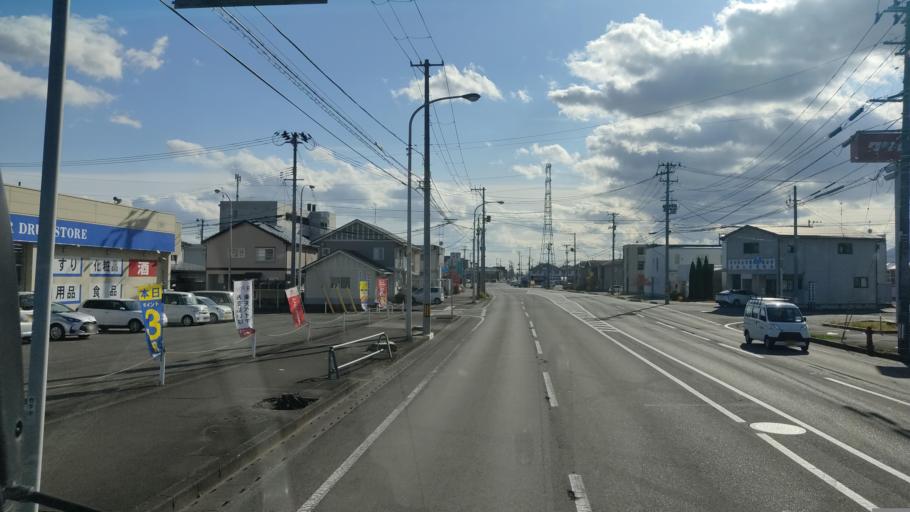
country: JP
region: Iwate
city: Morioka-shi
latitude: 39.6816
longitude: 141.1433
